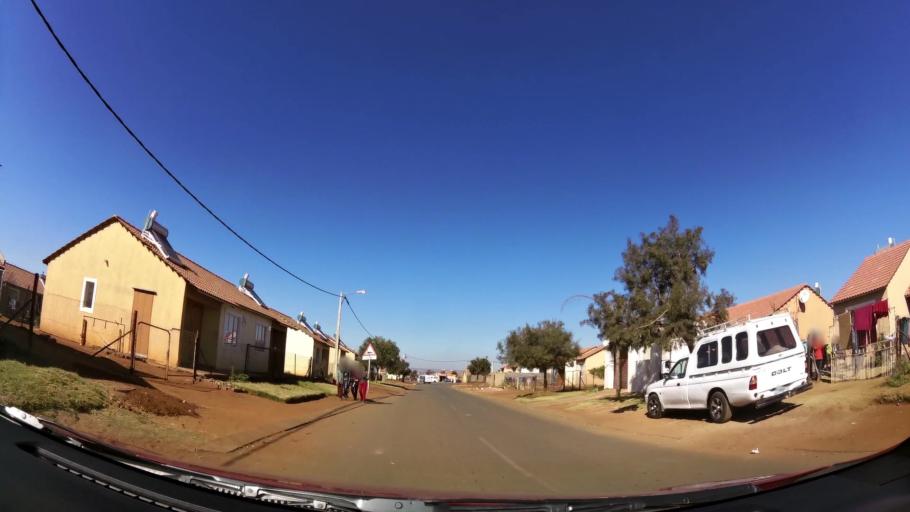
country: ZA
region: Gauteng
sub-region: City of Johannesburg Metropolitan Municipality
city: Soweto
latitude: -26.2357
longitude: 27.8027
